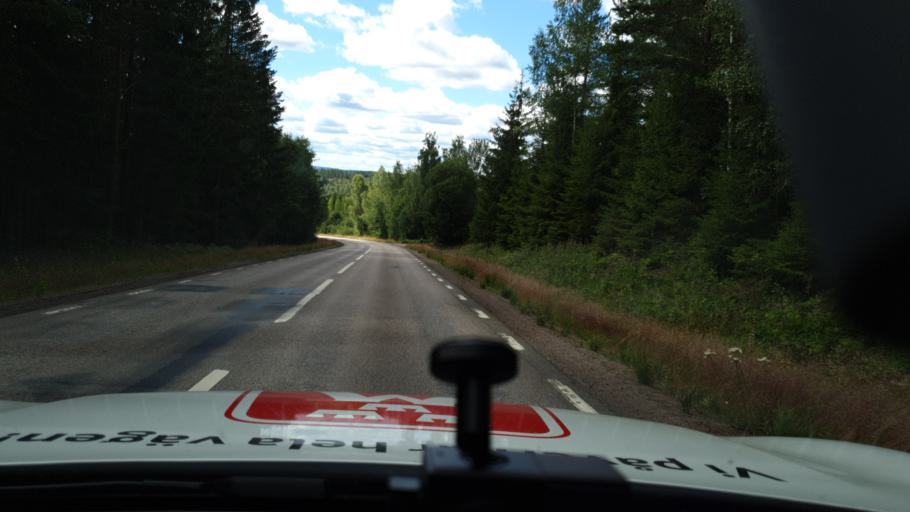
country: SE
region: Vaermland
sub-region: Sunne Kommun
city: Sunne
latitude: 59.6801
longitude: 13.0422
